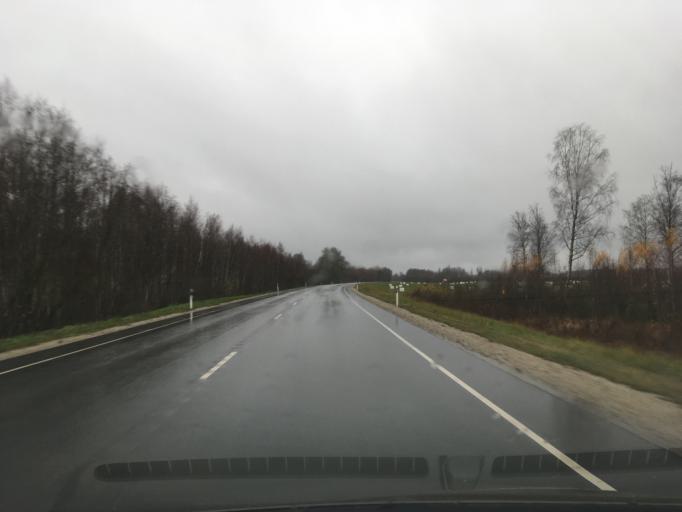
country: EE
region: Laeaene
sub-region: Lihula vald
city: Lihula
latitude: 58.8504
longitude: 24.0680
